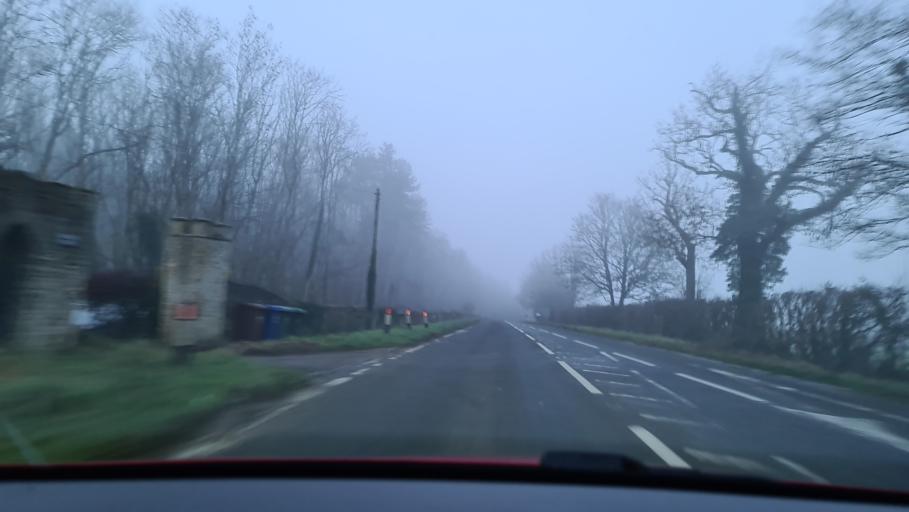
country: GB
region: England
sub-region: Oxfordshire
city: Bicester
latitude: 51.8952
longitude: -1.2262
